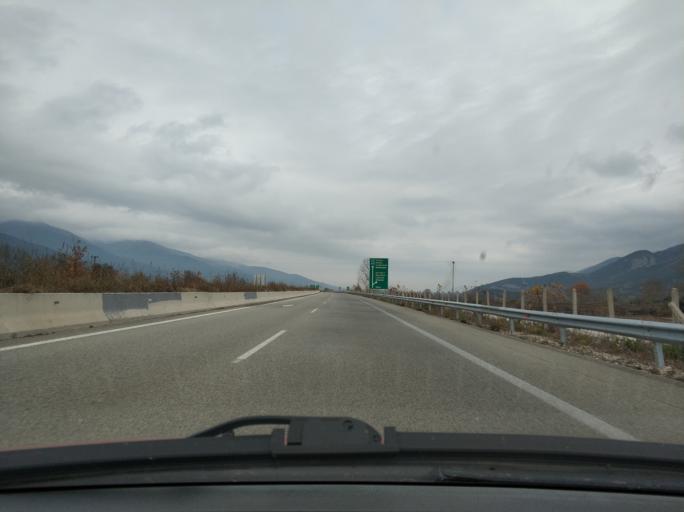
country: GR
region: East Macedonia and Thrace
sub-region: Nomos Kavalas
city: Nikisiani
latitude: 40.8336
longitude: 24.1075
